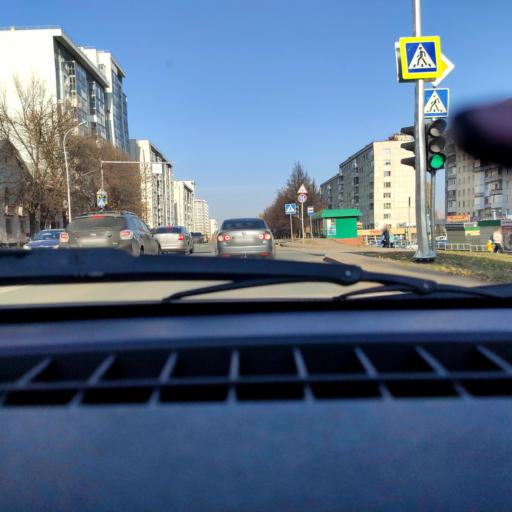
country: RU
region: Bashkortostan
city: Ufa
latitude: 54.7873
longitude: 56.0401
